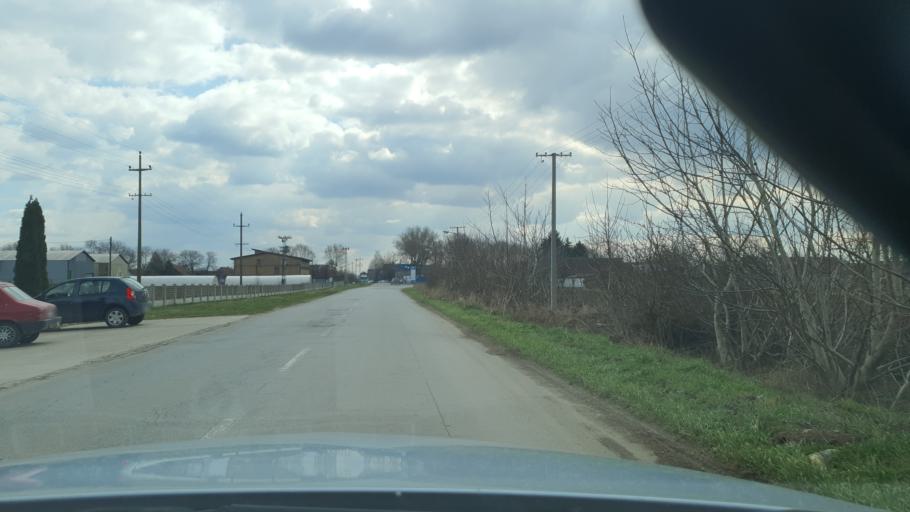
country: RS
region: Autonomna Pokrajina Vojvodina
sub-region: Juznobacki Okrug
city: Bac
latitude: 45.4171
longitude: 19.3135
